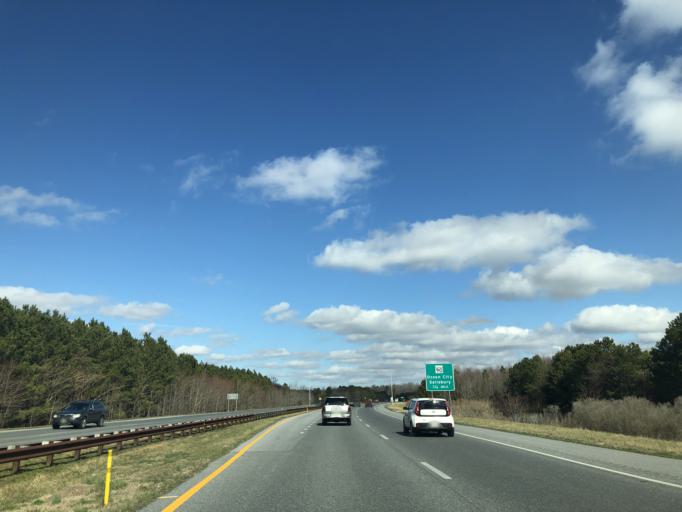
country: US
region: Maryland
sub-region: Worcester County
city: Berlin
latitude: 38.3617
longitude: -75.2131
